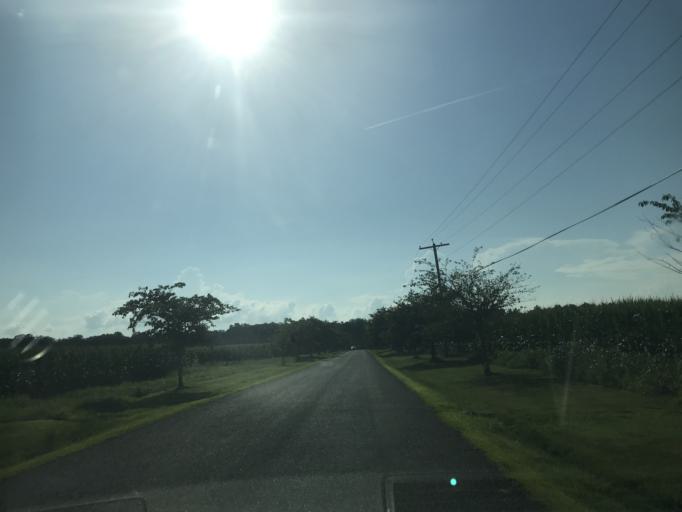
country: US
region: Maryland
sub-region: Harford County
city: Havre de Grace
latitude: 39.5215
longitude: -76.1167
